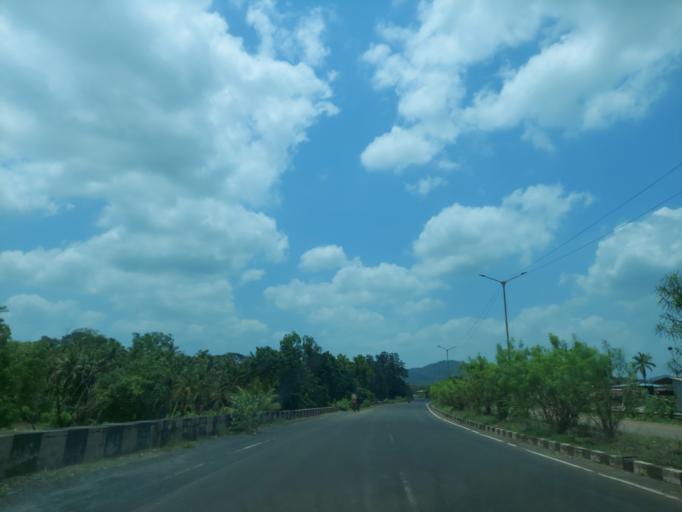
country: IN
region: Maharashtra
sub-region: Sindhudurg
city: Savantvadi
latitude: 15.8209
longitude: 73.8605
